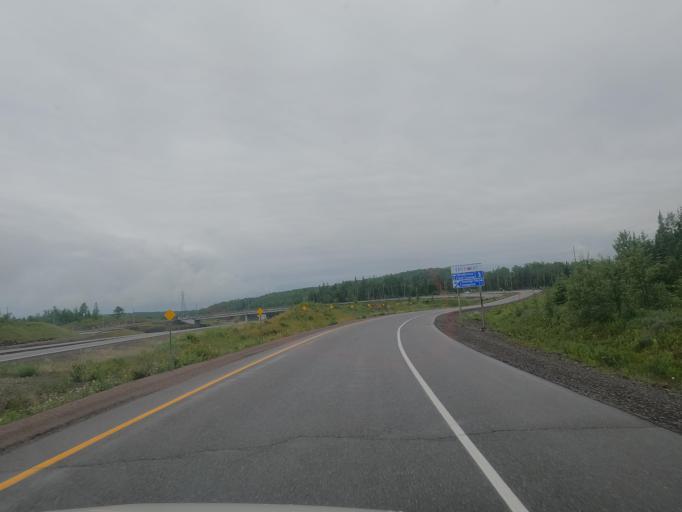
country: CA
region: Ontario
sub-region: Thunder Bay District
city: Thunder Bay
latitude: 48.4840
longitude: -89.1779
